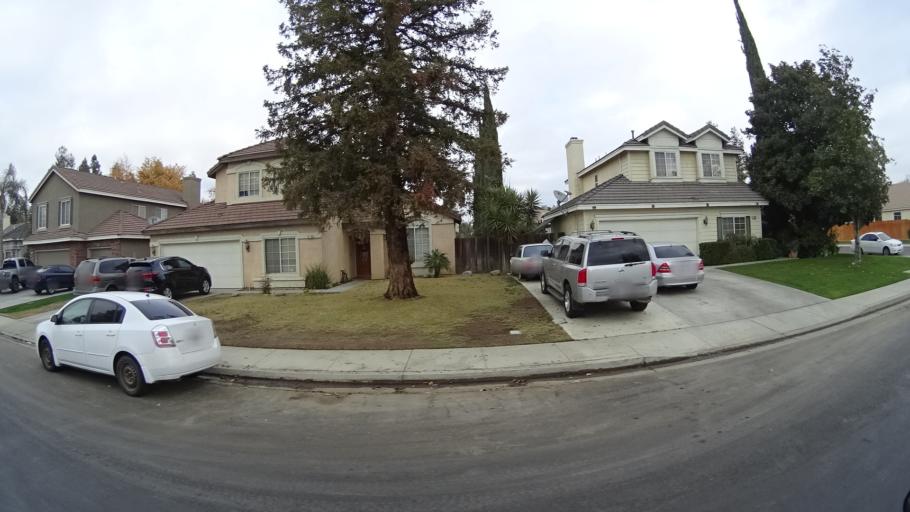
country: US
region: California
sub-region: Kern County
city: Greenacres
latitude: 35.3003
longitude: -119.0848
